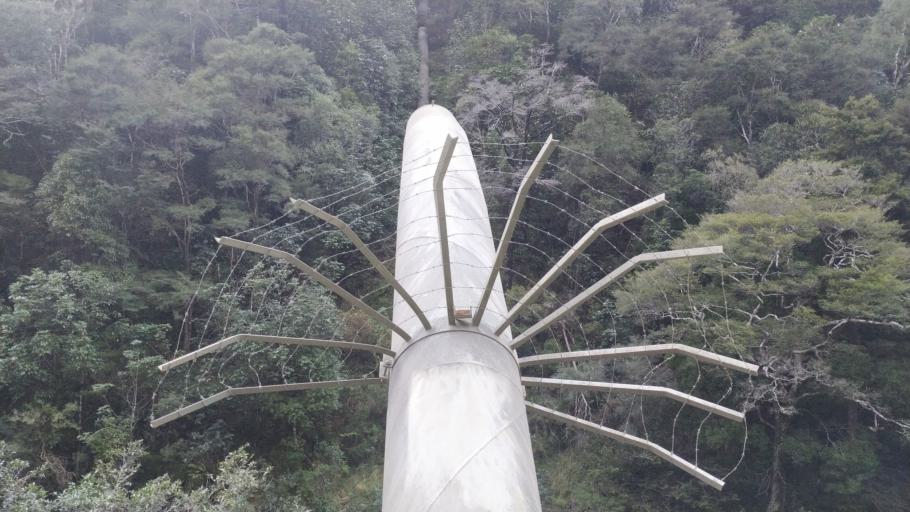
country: NZ
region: Nelson
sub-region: Nelson City
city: Nelson
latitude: -41.2918
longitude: 173.3441
